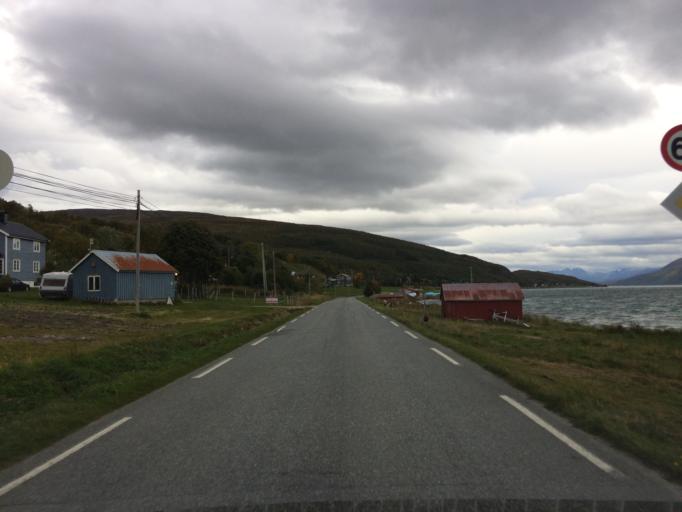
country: NO
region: Troms
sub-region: Sorreisa
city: Sorreisa
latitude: 69.5278
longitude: 18.2828
